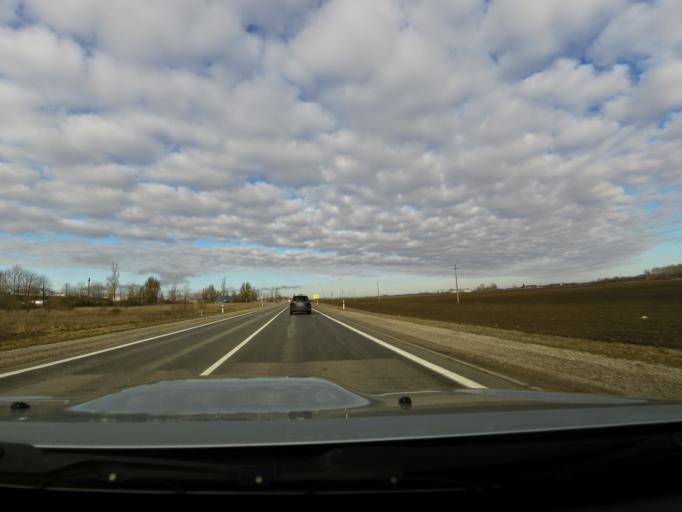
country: LT
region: Panevezys
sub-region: Panevezys City
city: Panevezys
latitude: 55.7484
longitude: 24.1521
